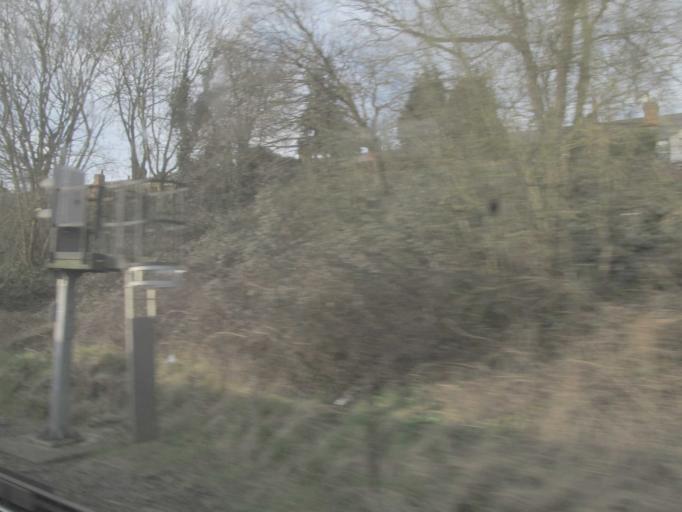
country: GB
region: England
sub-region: Wokingham
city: Earley
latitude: 51.4480
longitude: -0.9314
